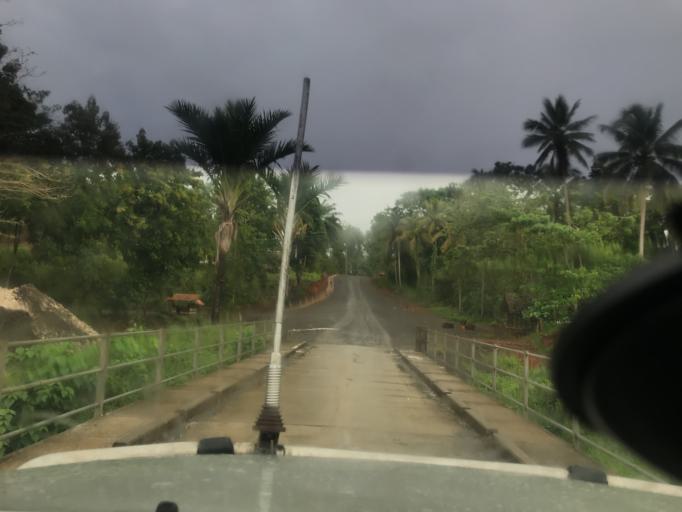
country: SB
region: Malaita
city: Auki
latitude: -8.9688
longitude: 160.7829
